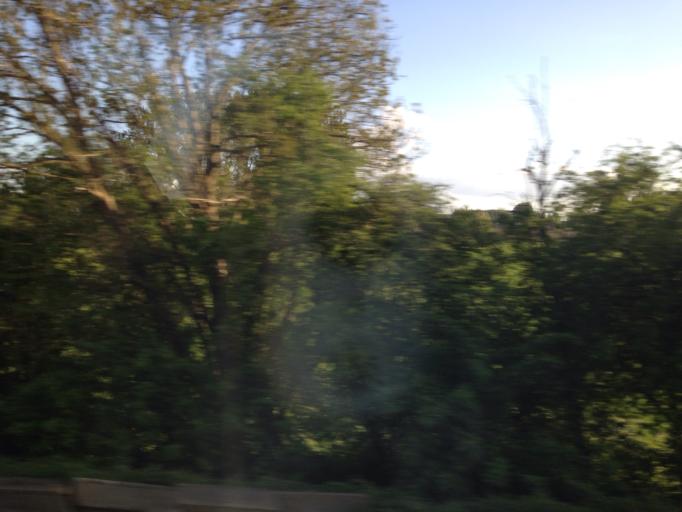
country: BE
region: Flanders
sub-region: Provincie Oost-Vlaanderen
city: Wetteren
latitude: 50.9622
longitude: 3.8763
